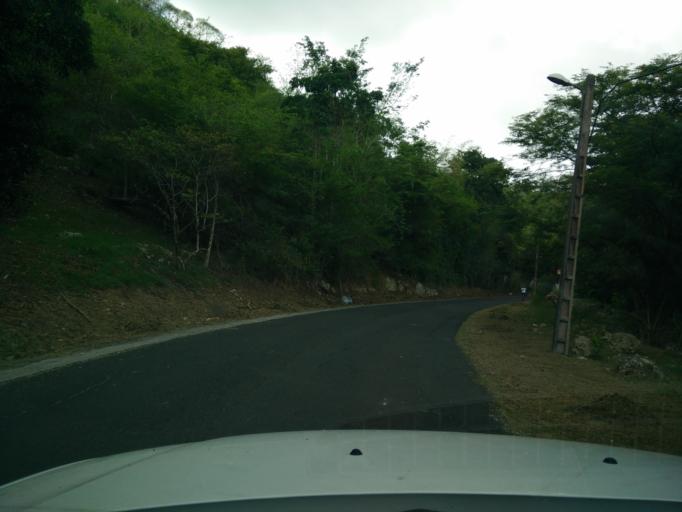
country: GP
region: Guadeloupe
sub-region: Guadeloupe
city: Le Gosier
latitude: 16.2249
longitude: -61.4629
